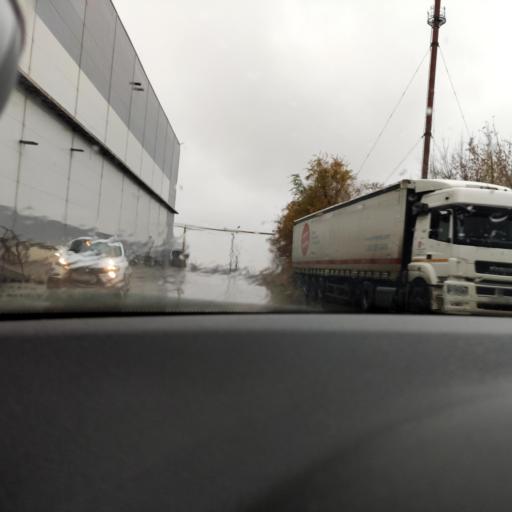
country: RU
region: Samara
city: Petra-Dubrava
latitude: 53.2746
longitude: 50.2722
